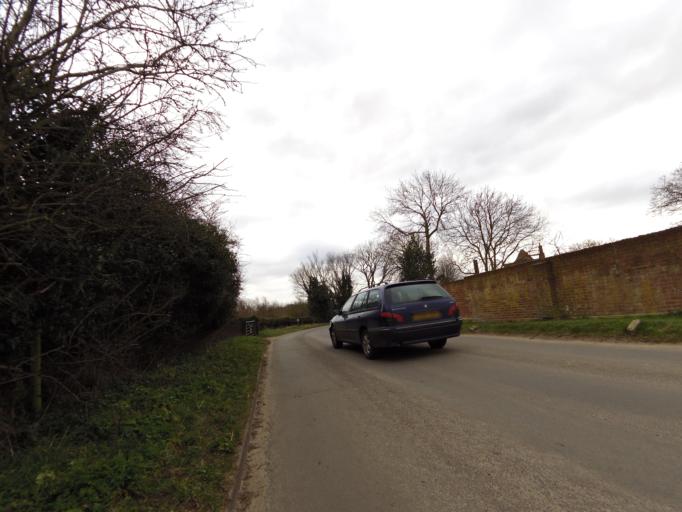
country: GB
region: England
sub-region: Suffolk
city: Woodbridge
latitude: 52.0389
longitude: 1.3137
